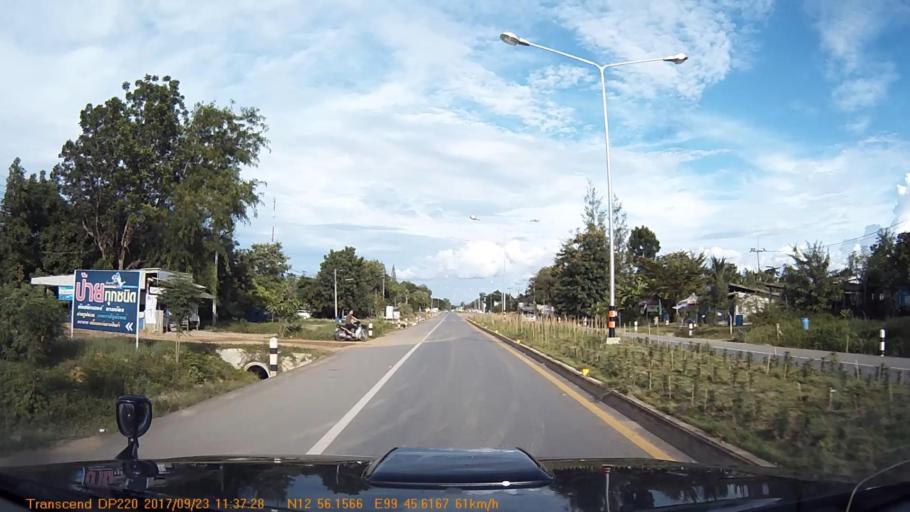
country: TH
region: Phetchaburi
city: Kaeng Krachan
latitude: 12.9359
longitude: 99.7603
